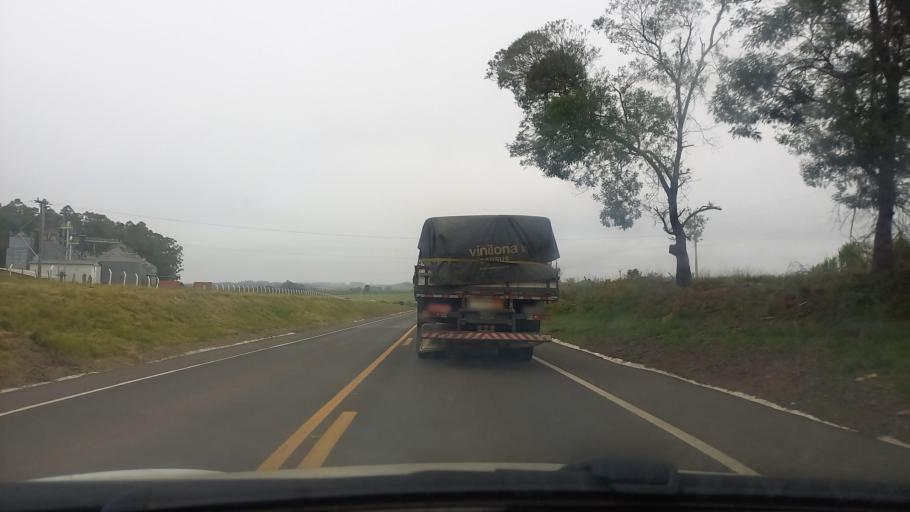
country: BR
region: Rio Grande do Sul
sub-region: Rosario Do Sul
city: Rosario do Sul
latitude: -30.2784
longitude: -54.9800
